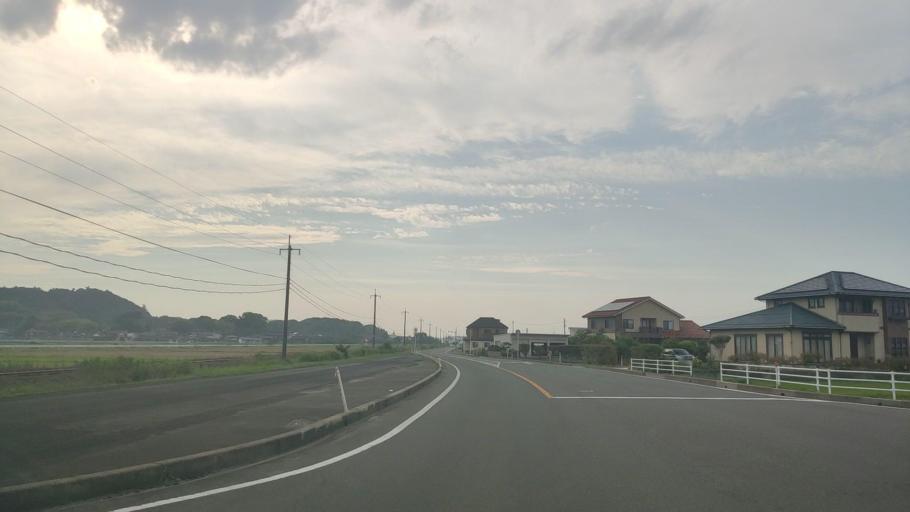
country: JP
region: Tottori
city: Kurayoshi
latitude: 35.4763
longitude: 133.8204
